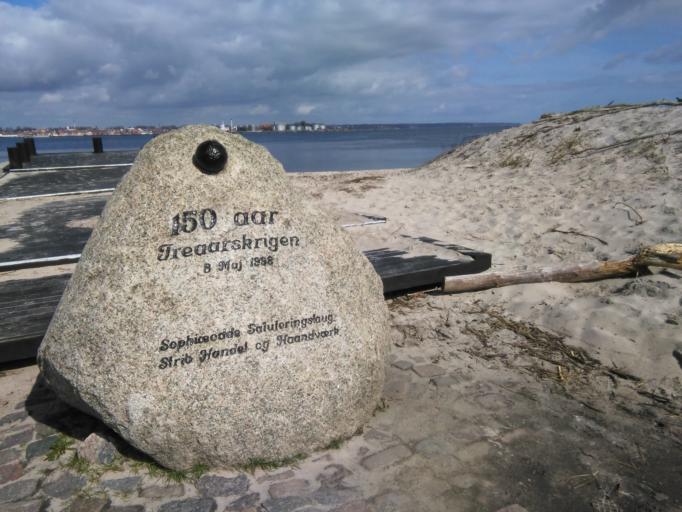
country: DK
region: South Denmark
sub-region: Middelfart Kommune
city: Strib
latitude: 55.5437
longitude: 9.7605
